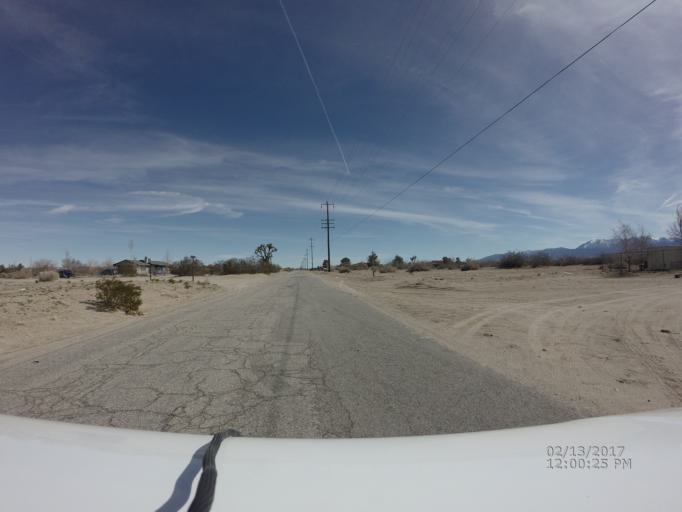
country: US
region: California
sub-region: Los Angeles County
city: Littlerock
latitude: 34.5579
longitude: -117.9299
